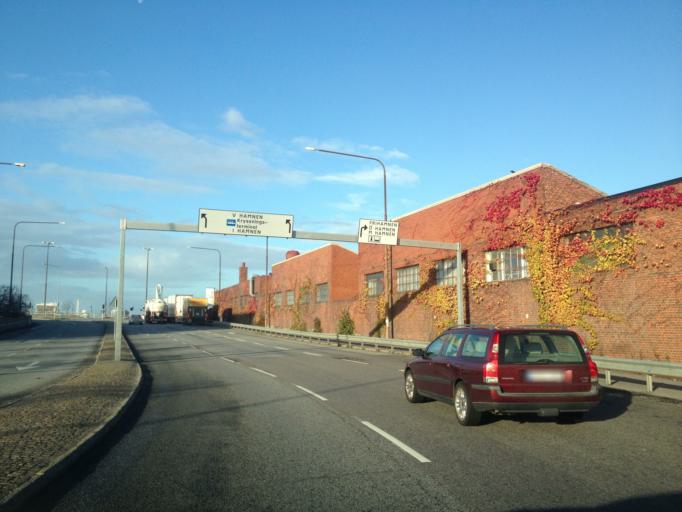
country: SE
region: Skane
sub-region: Malmo
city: Malmoe
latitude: 55.6151
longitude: 13.0229
